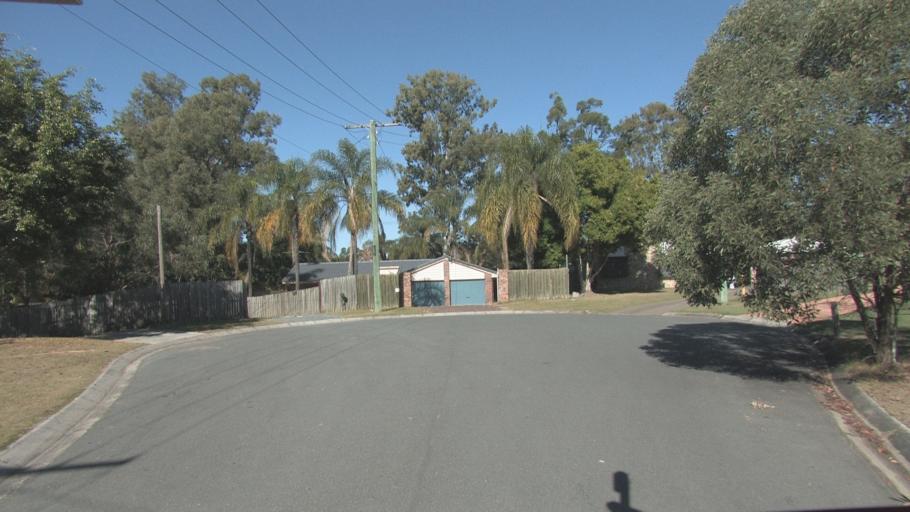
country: AU
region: Queensland
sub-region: Logan
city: Logan Reserve
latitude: -27.6806
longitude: 153.0663
